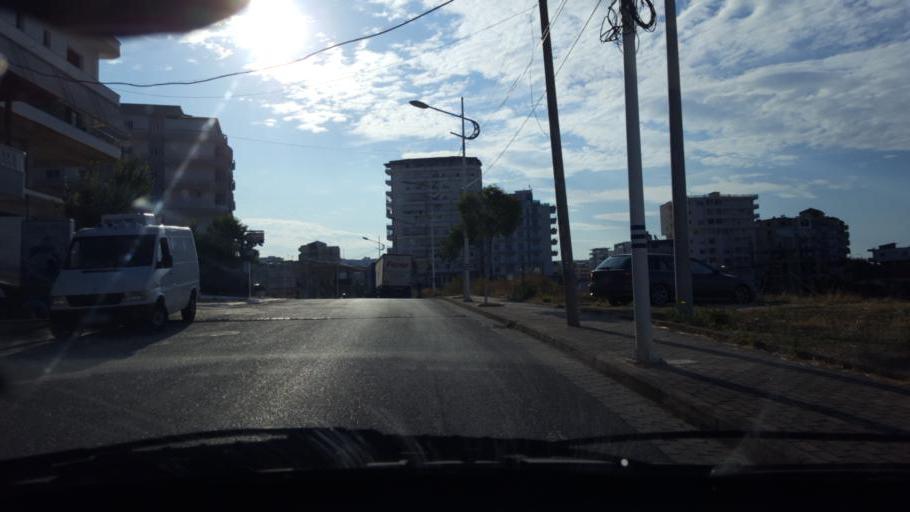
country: AL
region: Vlore
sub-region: Rrethi i Sarandes
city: Sarande
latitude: 39.8746
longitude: 19.9891
